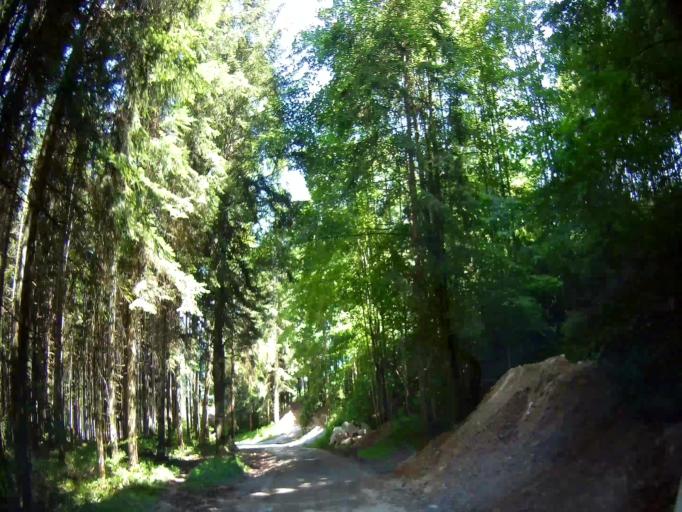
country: AT
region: Salzburg
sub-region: Politischer Bezirk Zell am See
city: Leogang
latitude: 47.4514
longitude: 12.7894
